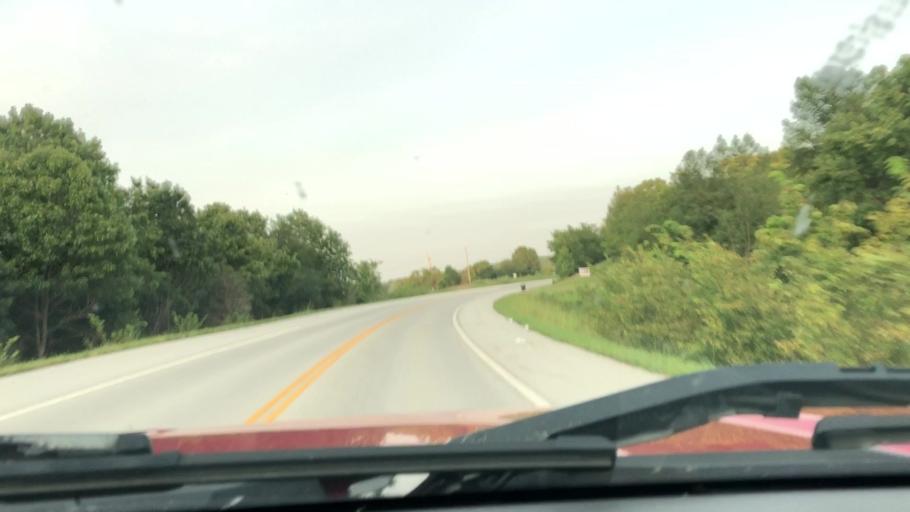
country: US
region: Missouri
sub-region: Jasper County
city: Duquesne
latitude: 36.9696
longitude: -94.4384
